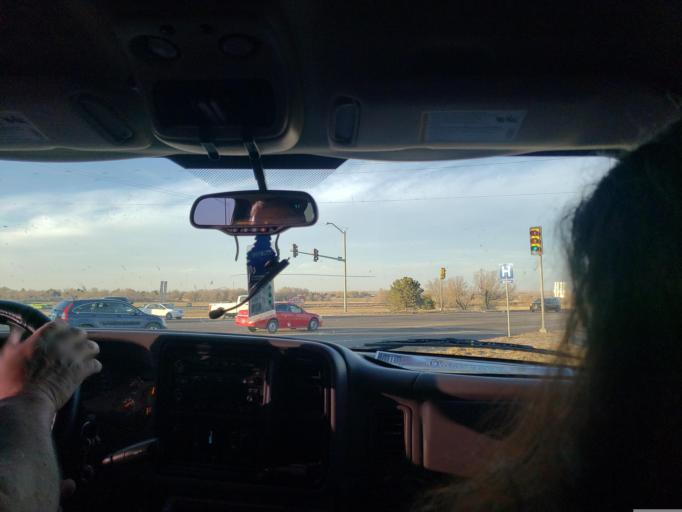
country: US
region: Oklahoma
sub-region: Texas County
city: Guymon
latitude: 36.6888
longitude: -101.4665
